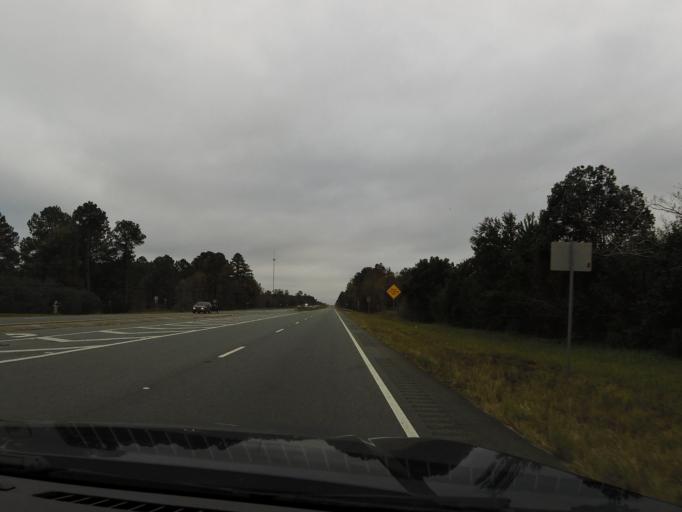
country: US
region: Georgia
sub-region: Charlton County
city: Folkston
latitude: 30.9093
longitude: -82.0741
